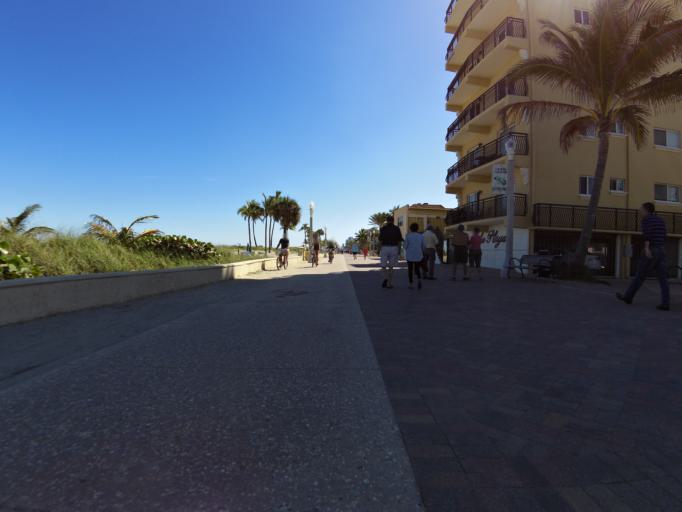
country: US
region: Florida
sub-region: Broward County
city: Hollywood
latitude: 26.0237
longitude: -80.1150
